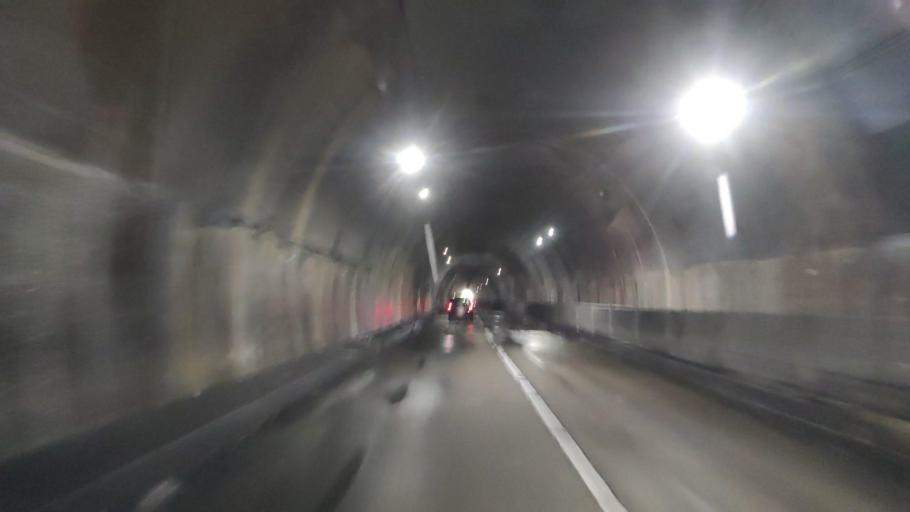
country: JP
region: Mie
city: Ise
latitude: 34.2717
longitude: 136.4906
